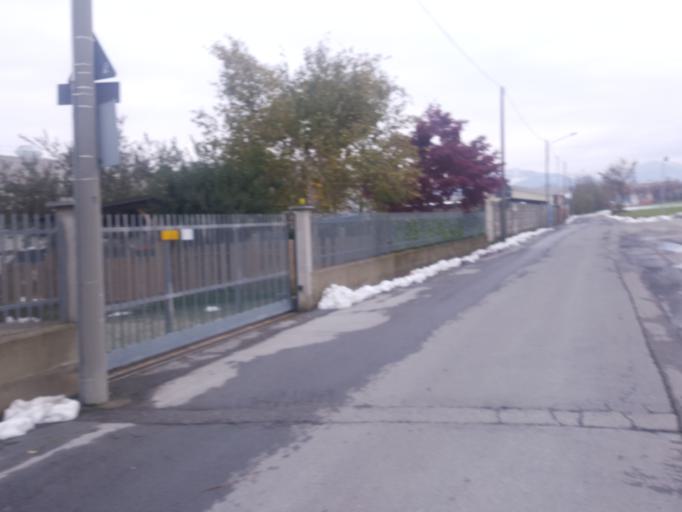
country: IT
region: Piedmont
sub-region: Provincia di Cuneo
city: Breo
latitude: 44.4020
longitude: 7.8240
